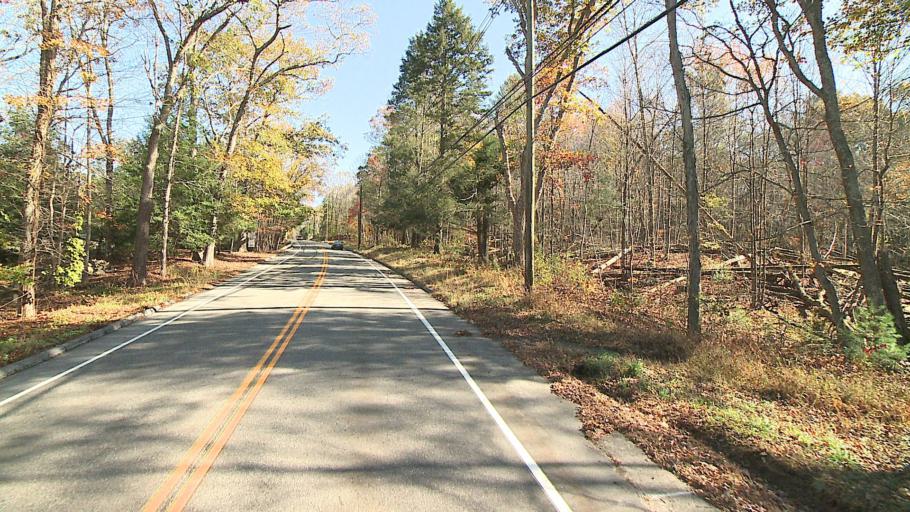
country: US
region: Connecticut
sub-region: Tolland County
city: Storrs
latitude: 41.8345
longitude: -72.2385
